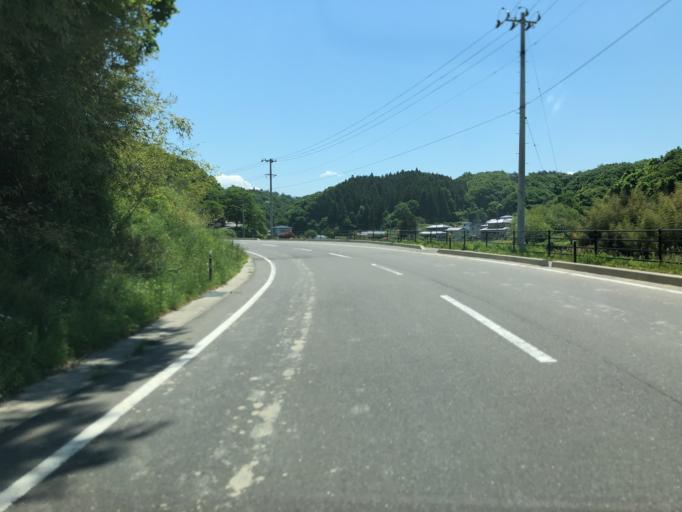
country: JP
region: Fukushima
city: Miharu
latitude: 37.5011
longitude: 140.4761
